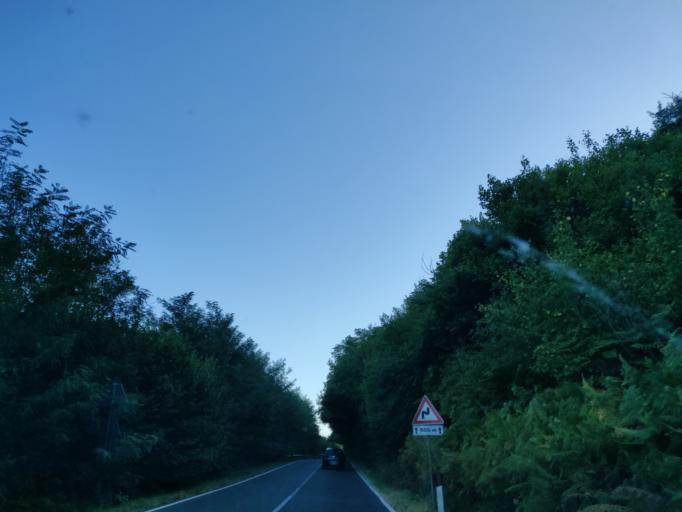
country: IT
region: Latium
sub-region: Provincia di Viterbo
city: Gradoli
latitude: 42.6544
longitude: 11.8459
